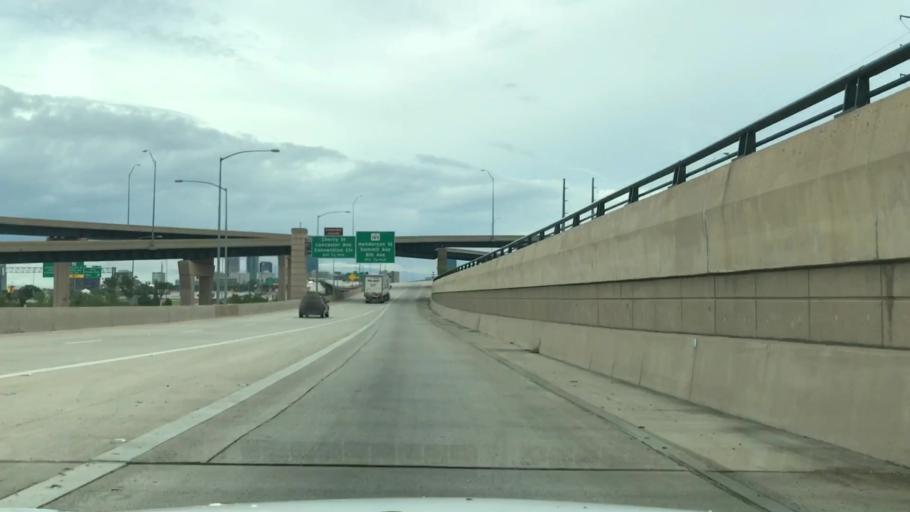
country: US
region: Texas
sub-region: Tarrant County
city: Fort Worth
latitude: 32.7333
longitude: -97.3582
